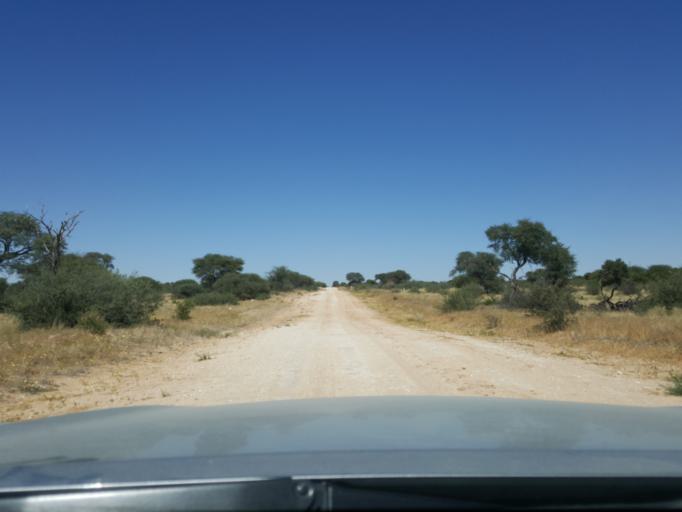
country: BW
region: Kgalagadi
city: Hukuntsi
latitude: -24.0208
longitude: 21.2159
